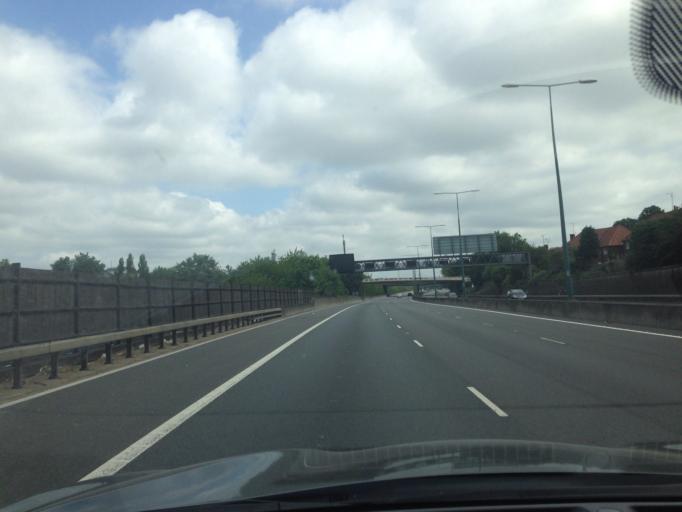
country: GB
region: England
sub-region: Greater London
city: Hendon
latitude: 51.5852
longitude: -0.2380
